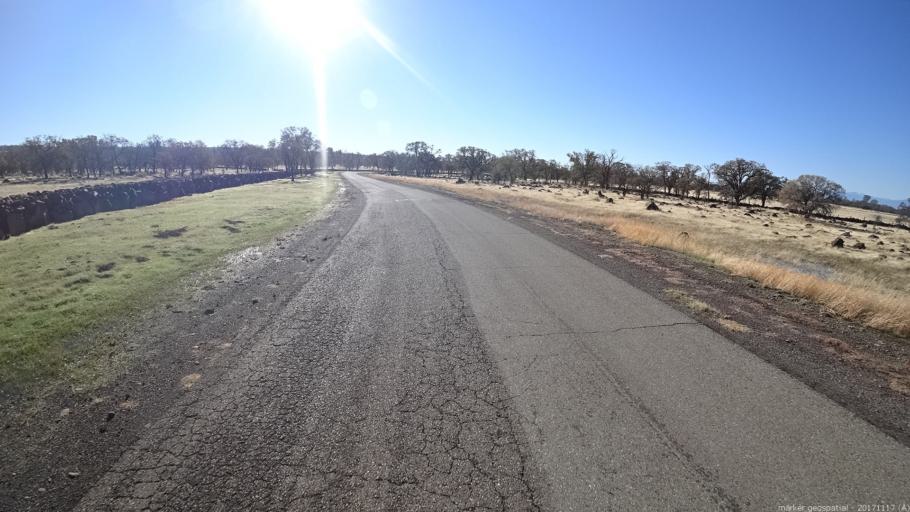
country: US
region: California
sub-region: Shasta County
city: Palo Cedro
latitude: 40.4593
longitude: -122.1036
